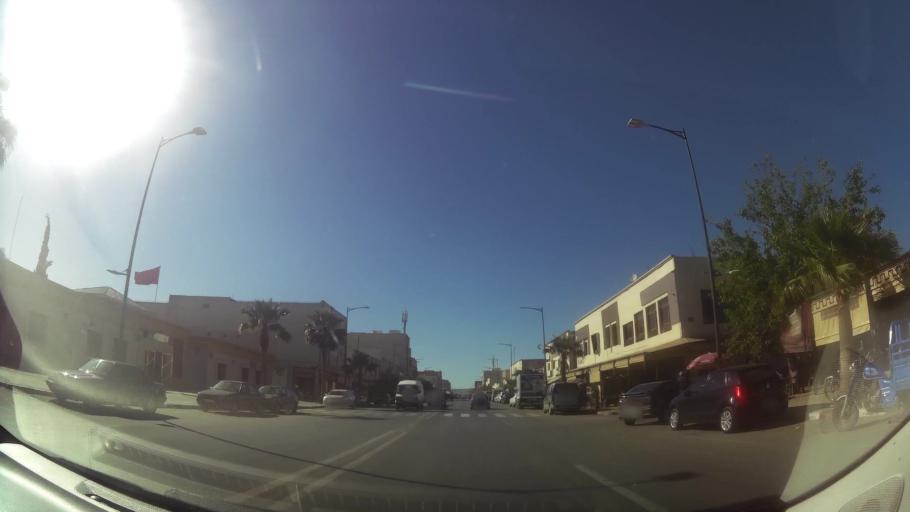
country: MA
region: Oriental
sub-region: Berkane-Taourirt
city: Ahfir
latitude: 34.8587
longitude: -1.9934
